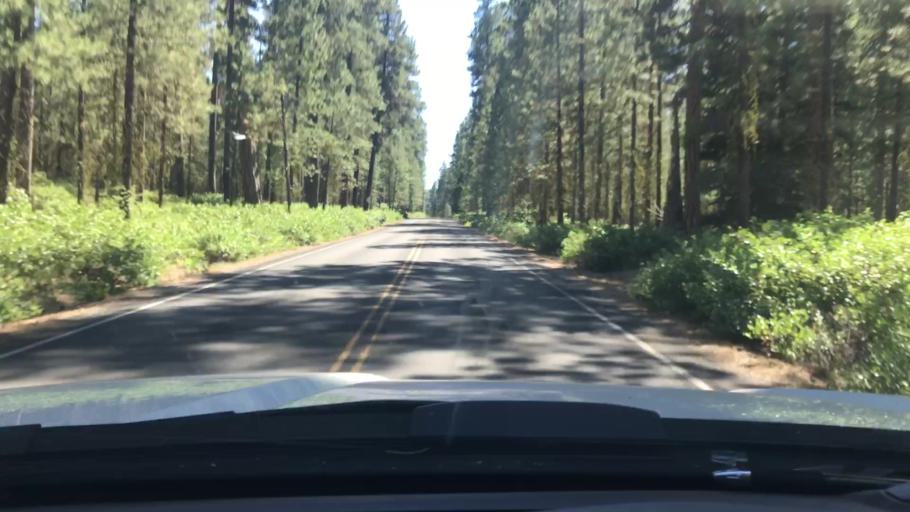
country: US
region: Oregon
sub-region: Deschutes County
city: Sisters
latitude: 44.4223
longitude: -121.6677
